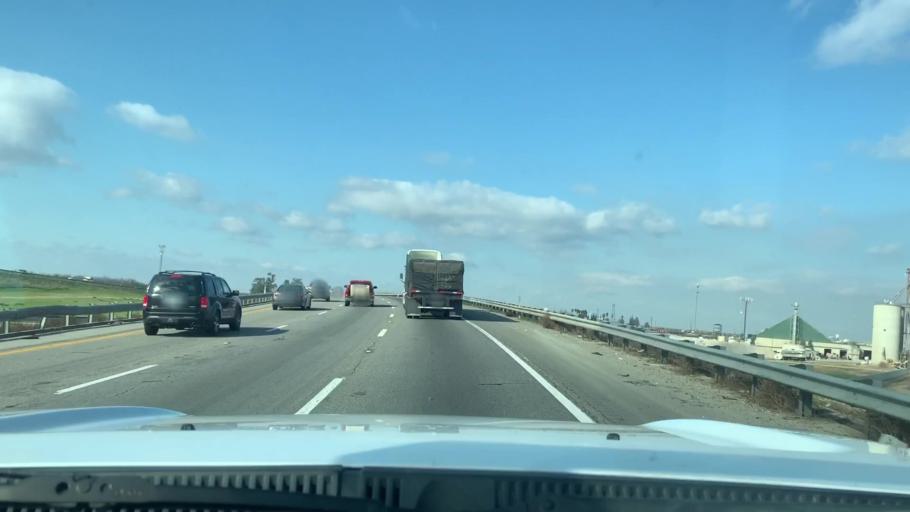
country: US
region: California
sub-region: Kern County
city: McFarland
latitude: 35.5919
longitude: -119.2052
